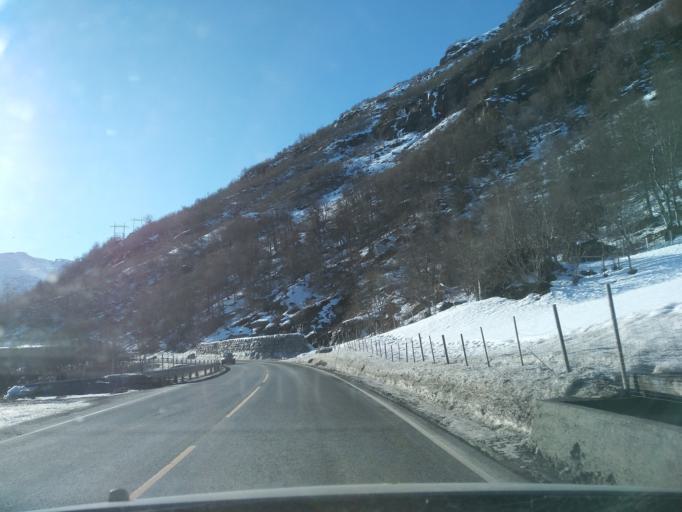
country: NO
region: Hordaland
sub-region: Odda
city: Odda
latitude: 59.8261
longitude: 6.7984
